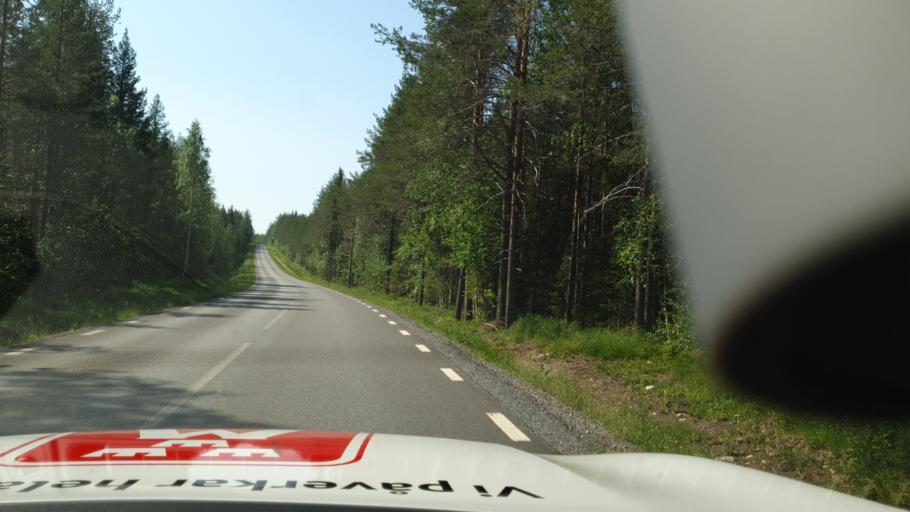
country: SE
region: Vaesterbotten
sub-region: Skelleftea Kommun
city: Langsele
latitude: 64.9751
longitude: 20.0523
